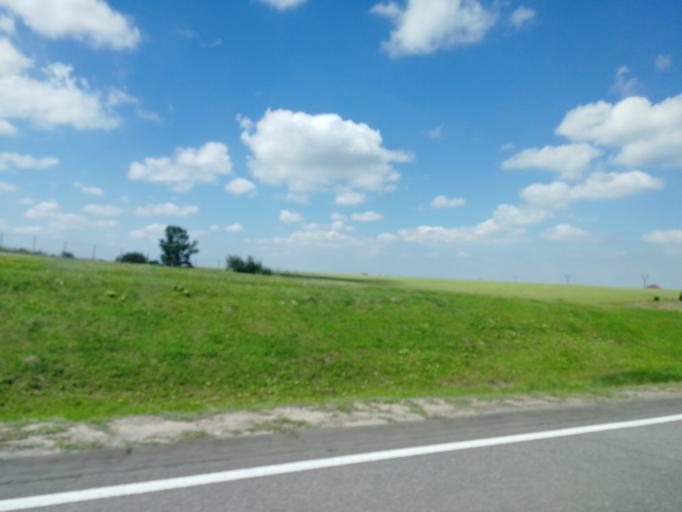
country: RU
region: Tula
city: Dubovka
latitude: 53.9281
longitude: 38.0380
